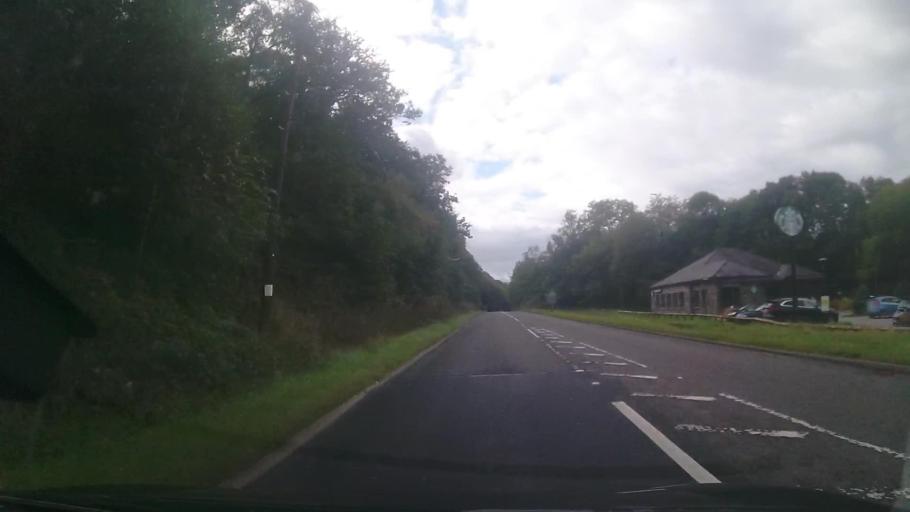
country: GB
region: Wales
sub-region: Gwynedd
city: Dolgellau
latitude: 52.7460
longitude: -3.8612
